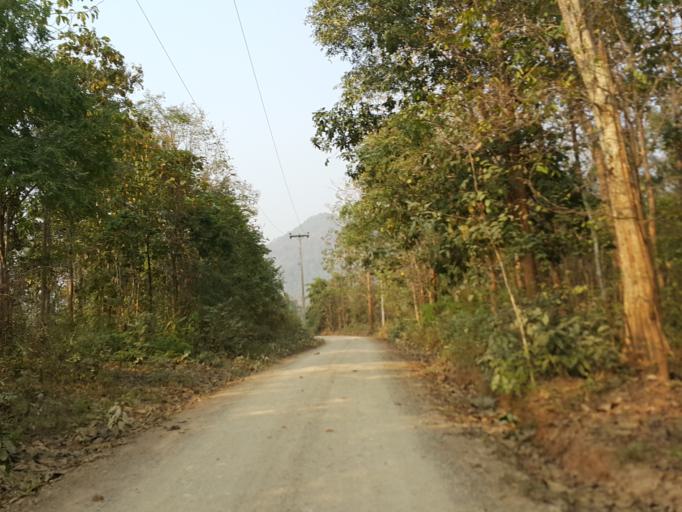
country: TH
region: Lamphun
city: Li
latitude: 17.6021
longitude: 98.9711
